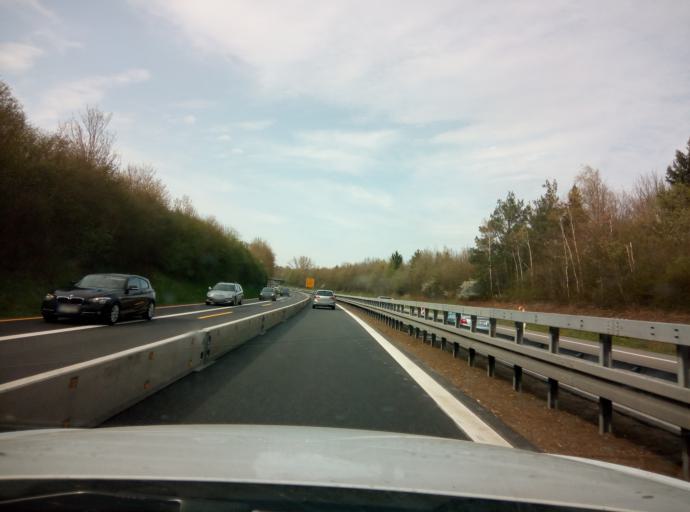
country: DE
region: Baden-Wuerttemberg
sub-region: Tuebingen Region
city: Pliezhausen
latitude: 48.5702
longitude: 9.1768
